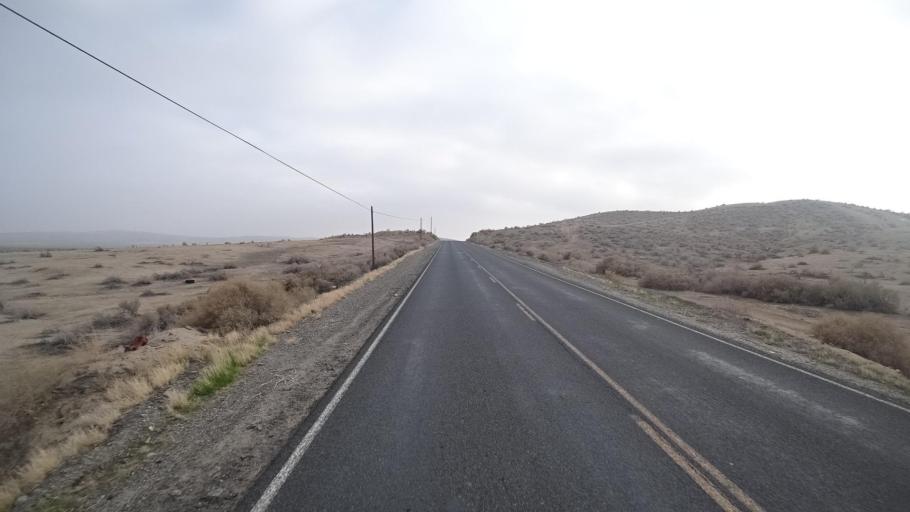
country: US
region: California
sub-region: Kern County
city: Ford City
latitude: 35.1933
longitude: -119.4457
